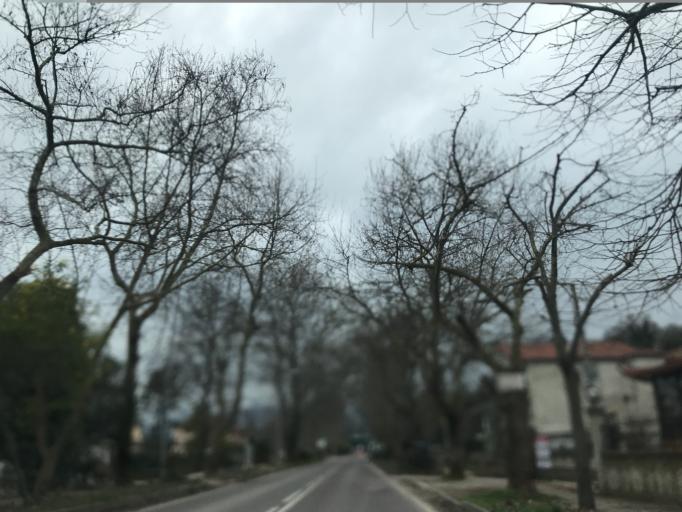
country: TR
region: Yalova
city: Kadikoy
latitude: 40.6385
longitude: 29.2267
